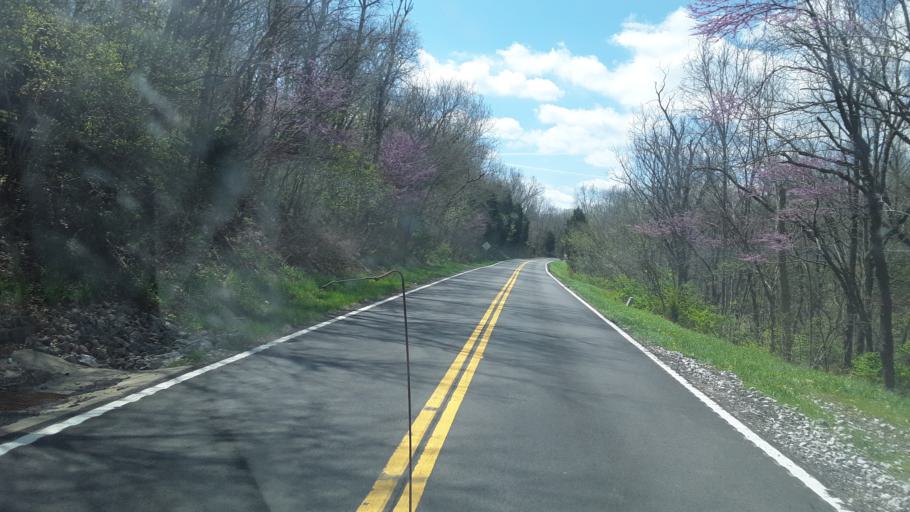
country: US
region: Kentucky
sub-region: Grant County
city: Dry Ridge
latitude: 38.6569
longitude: -84.6763
